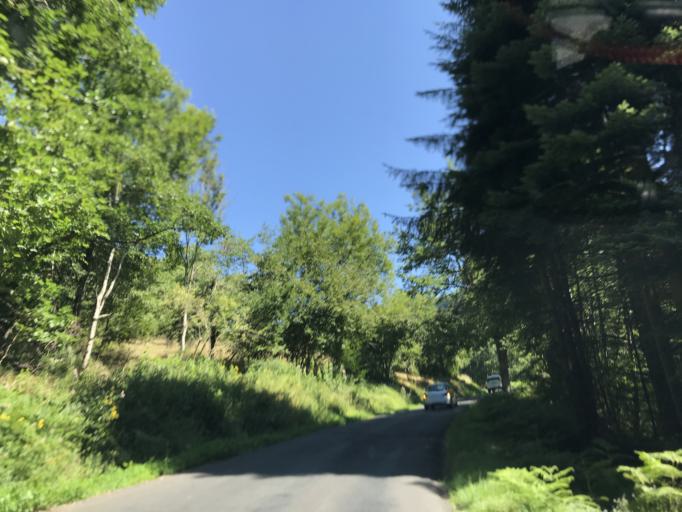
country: FR
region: Auvergne
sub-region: Departement du Puy-de-Dome
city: Job
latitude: 45.6692
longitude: 3.7280
